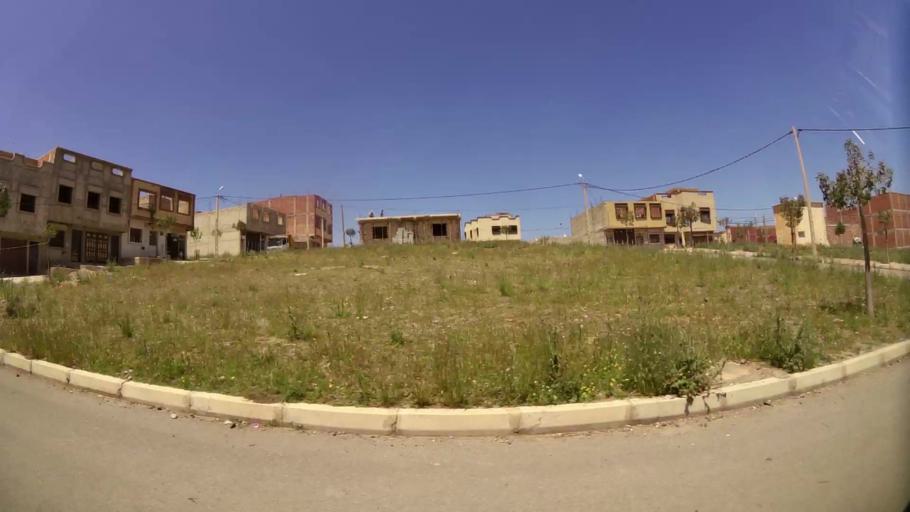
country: MA
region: Oriental
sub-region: Oujda-Angad
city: Oujda
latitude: 34.6747
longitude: -1.9517
